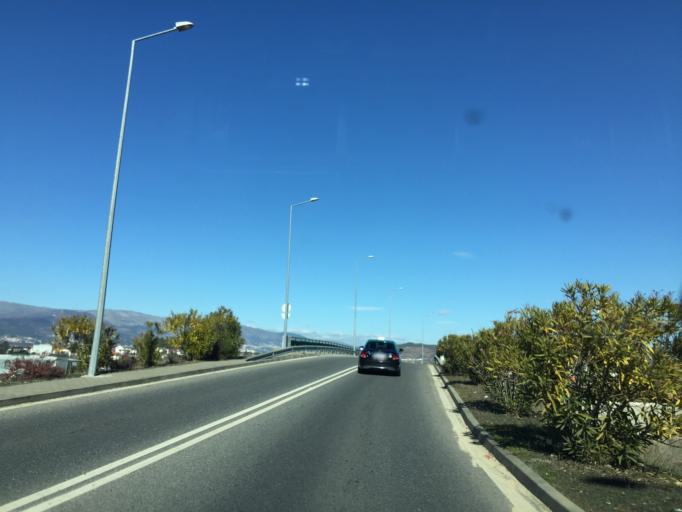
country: PT
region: Castelo Branco
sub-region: Concelho do Fundao
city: Fundao
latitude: 40.1602
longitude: -7.4977
